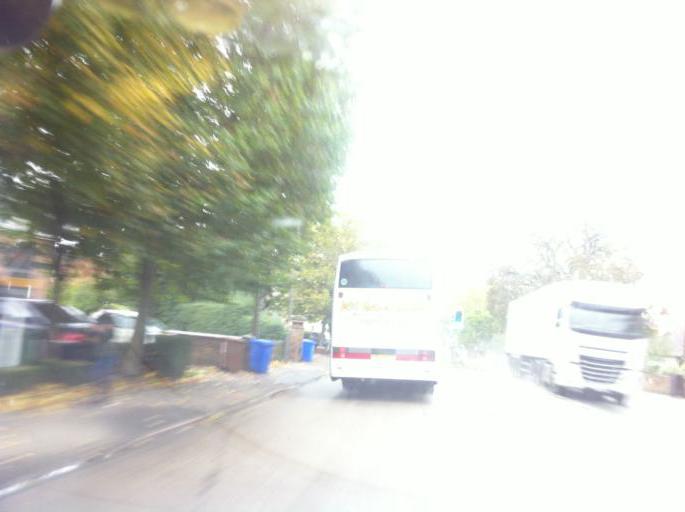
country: GB
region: England
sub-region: Lincolnshire
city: Boston
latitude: 52.9843
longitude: -0.0139
